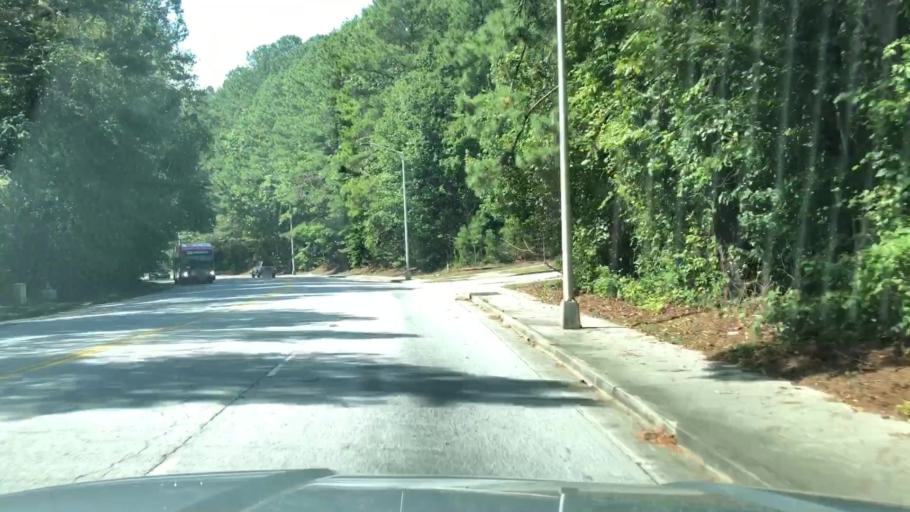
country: US
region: Georgia
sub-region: Fulton County
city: College Park
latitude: 33.6841
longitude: -84.5015
